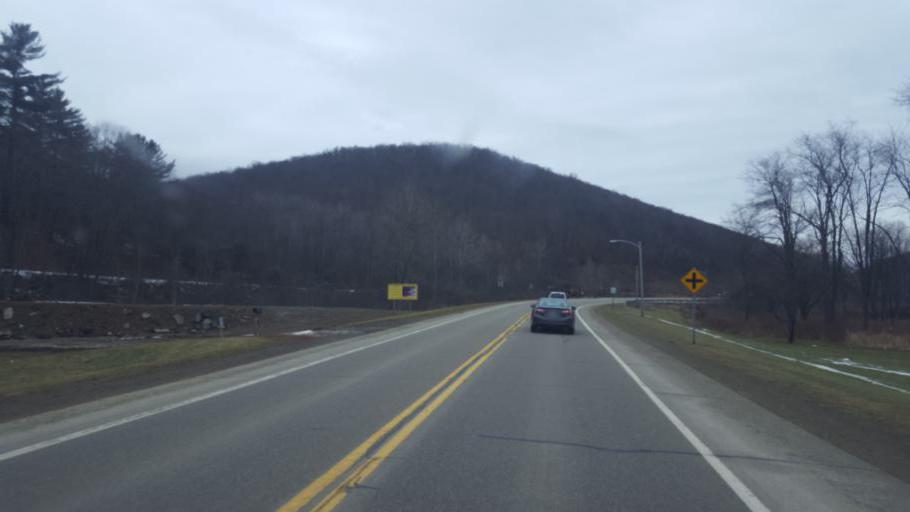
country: US
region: Pennsylvania
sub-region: Potter County
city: Coudersport
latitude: 41.7896
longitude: -78.0177
